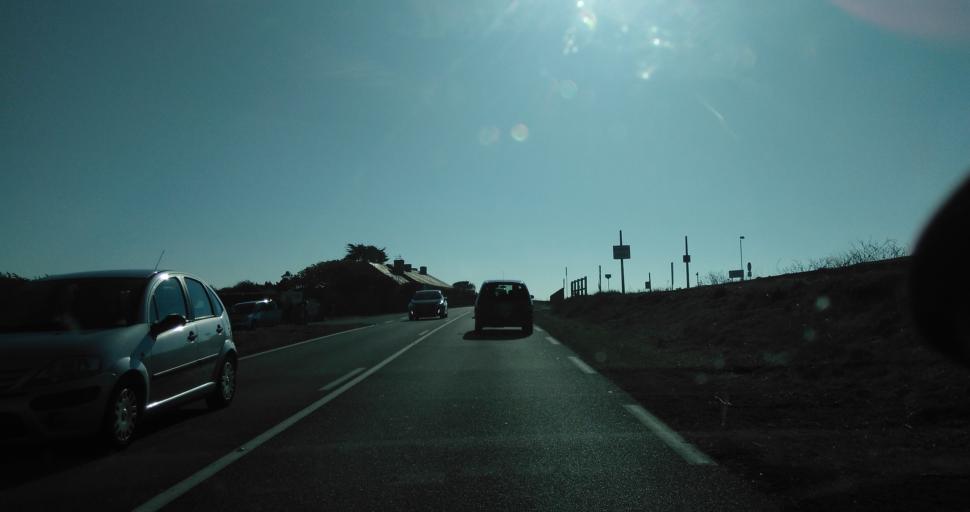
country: FR
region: Brittany
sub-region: Departement du Morbihan
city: Saint-Pierre-Quiberon
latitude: 47.5432
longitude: -3.1345
